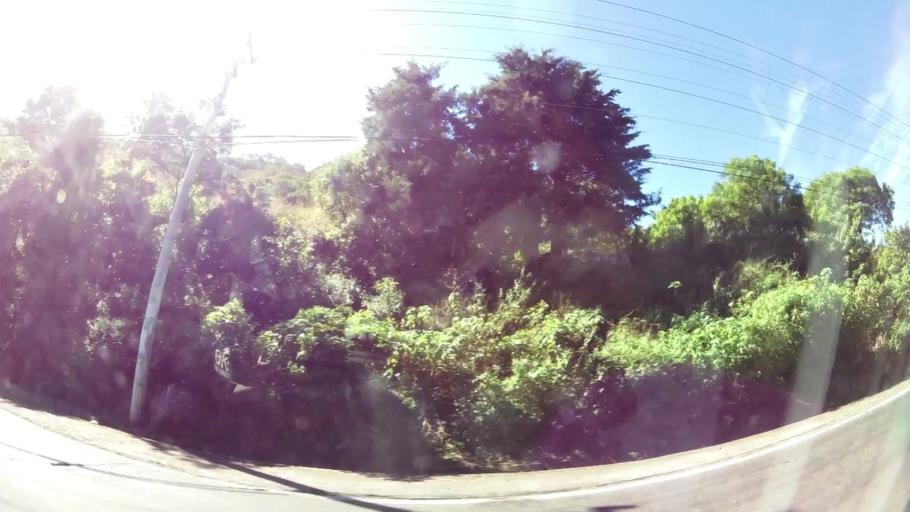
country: SV
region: Sonsonate
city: Juayua
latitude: 13.8539
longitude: -89.7743
